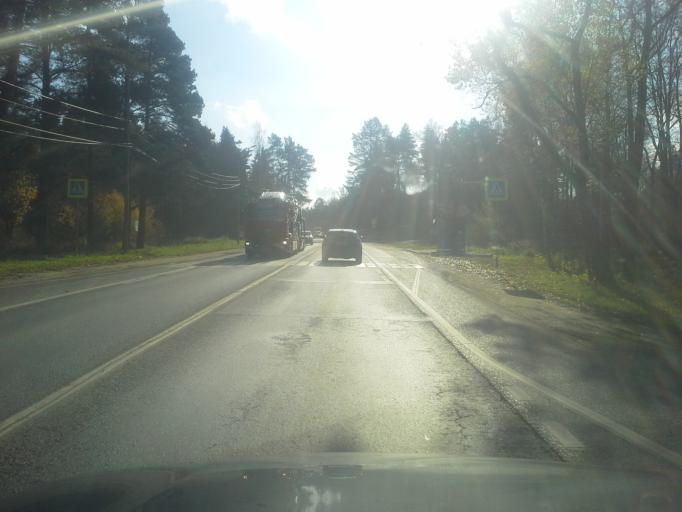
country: RU
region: Moskovskaya
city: Bol'shiye Vyazemy
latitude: 55.6491
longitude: 36.9724
